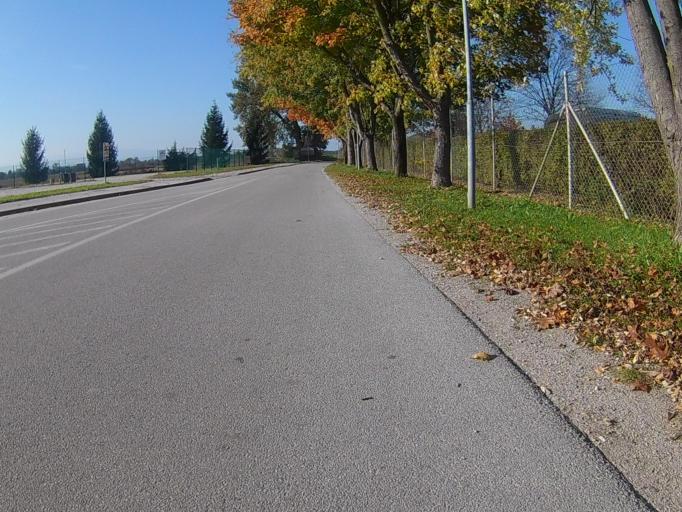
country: SI
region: Hajdina
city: Spodnja Hajdina
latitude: 46.4225
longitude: 15.8538
